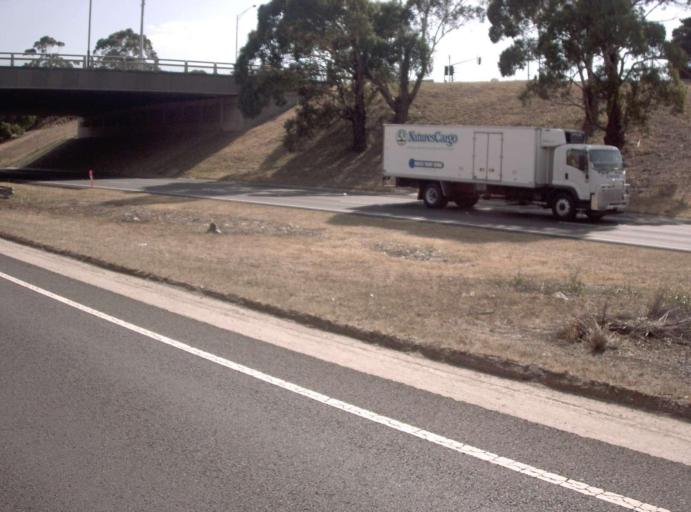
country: AU
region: Victoria
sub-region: Casey
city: Eumemmerring
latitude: -38.0042
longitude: 145.2517
